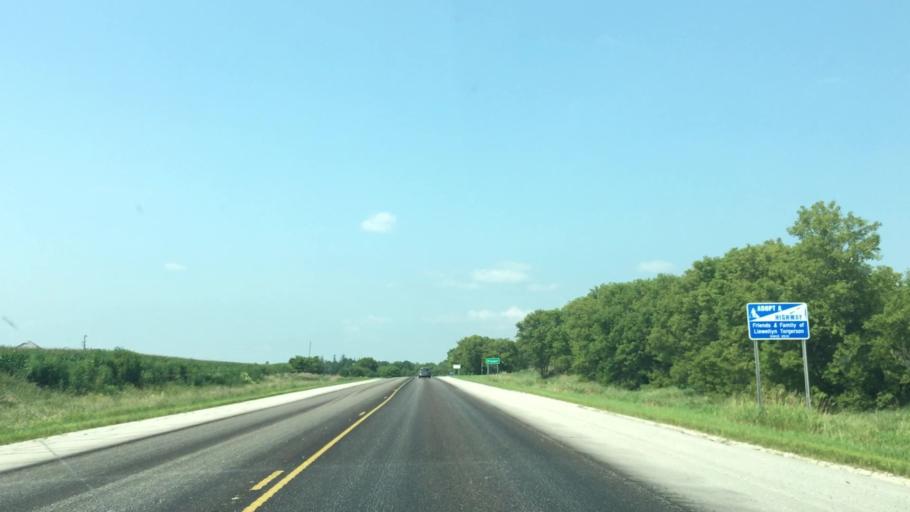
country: US
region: Minnesota
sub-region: Fillmore County
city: Harmony
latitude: 43.5021
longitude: -91.8712
